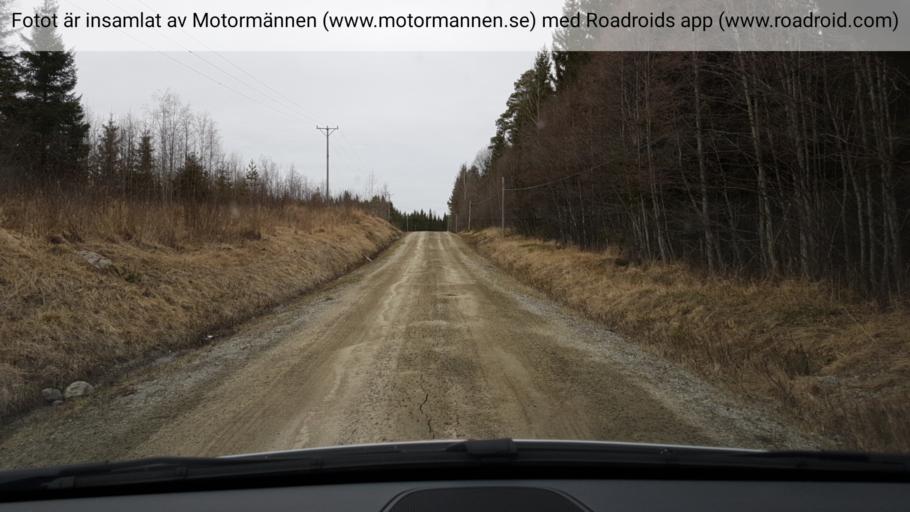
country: SE
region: Jaemtland
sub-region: Bergs Kommun
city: Hoverberg
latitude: 62.8735
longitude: 14.6177
